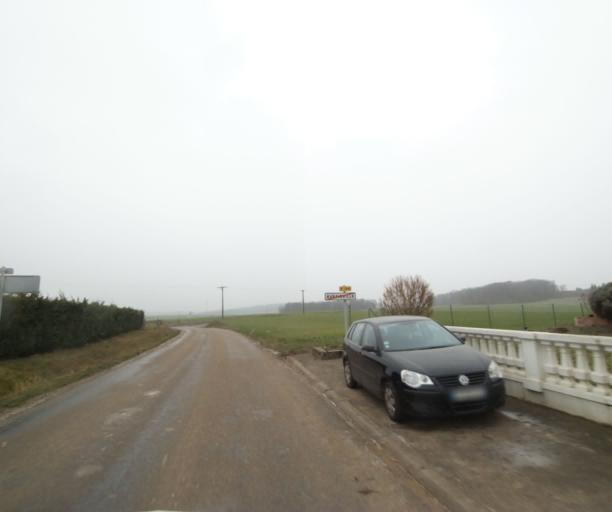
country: FR
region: Champagne-Ardenne
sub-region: Departement de la Haute-Marne
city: Bienville
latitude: 48.5289
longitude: 5.0445
